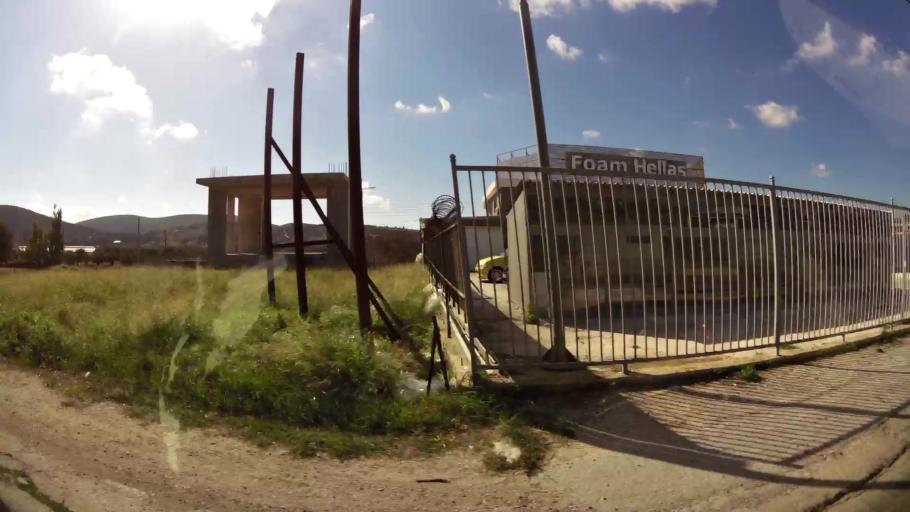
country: GR
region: Attica
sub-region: Nomarchia Anatolikis Attikis
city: Koropi
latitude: 37.8891
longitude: 23.8909
